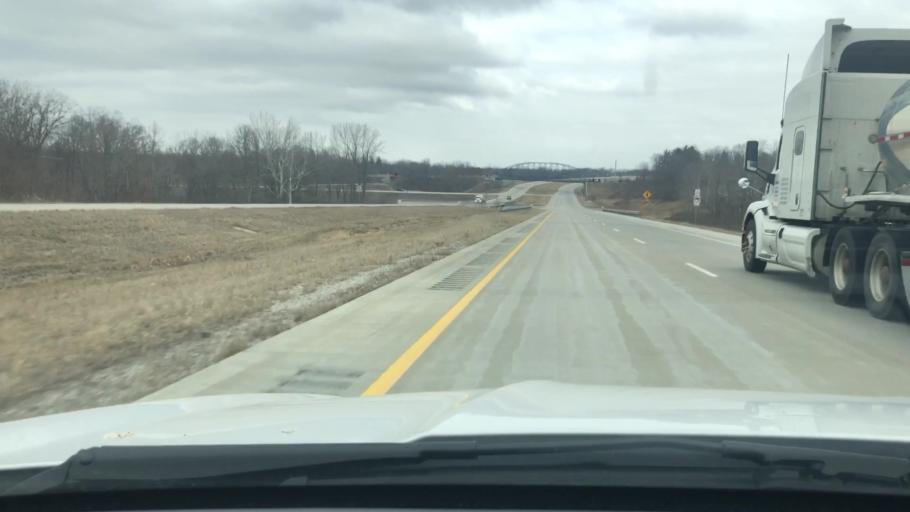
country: US
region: Indiana
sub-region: Carroll County
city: Delphi
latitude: 40.5888
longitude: -86.6520
